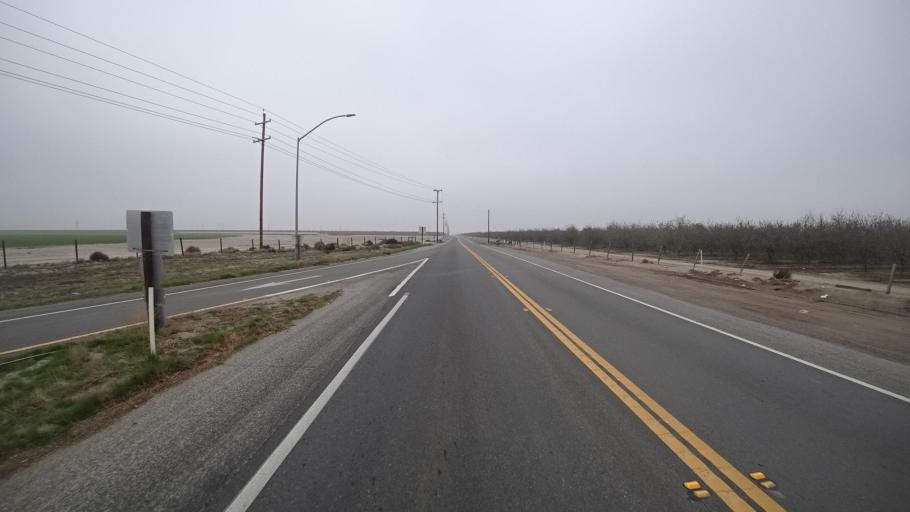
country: US
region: California
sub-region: Kern County
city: Greenfield
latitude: 35.2091
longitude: -119.1597
